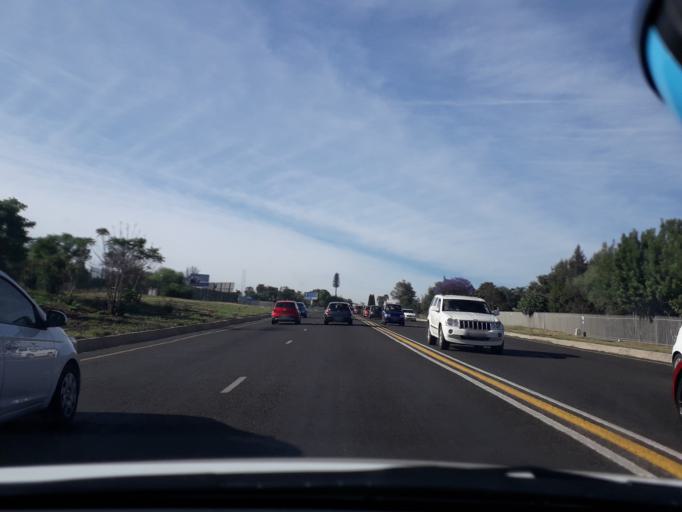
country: ZA
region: Gauteng
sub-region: City of Johannesburg Metropolitan Municipality
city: Roodepoort
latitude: -26.0988
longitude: 27.9266
